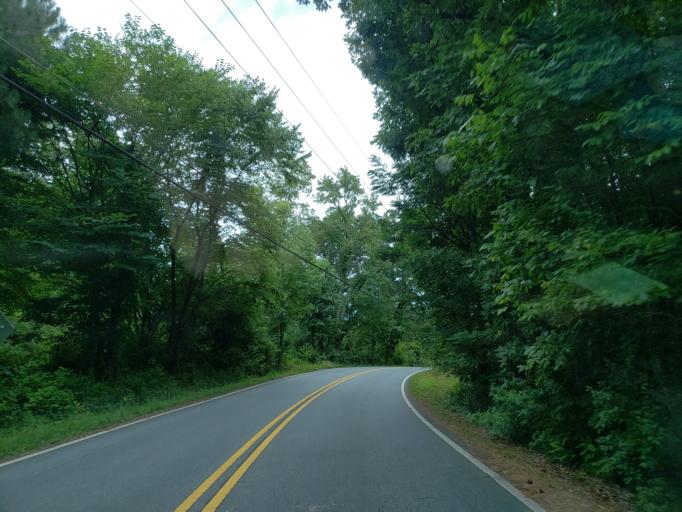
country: US
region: Georgia
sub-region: Cobb County
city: Acworth
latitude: 34.0168
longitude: -84.6865
